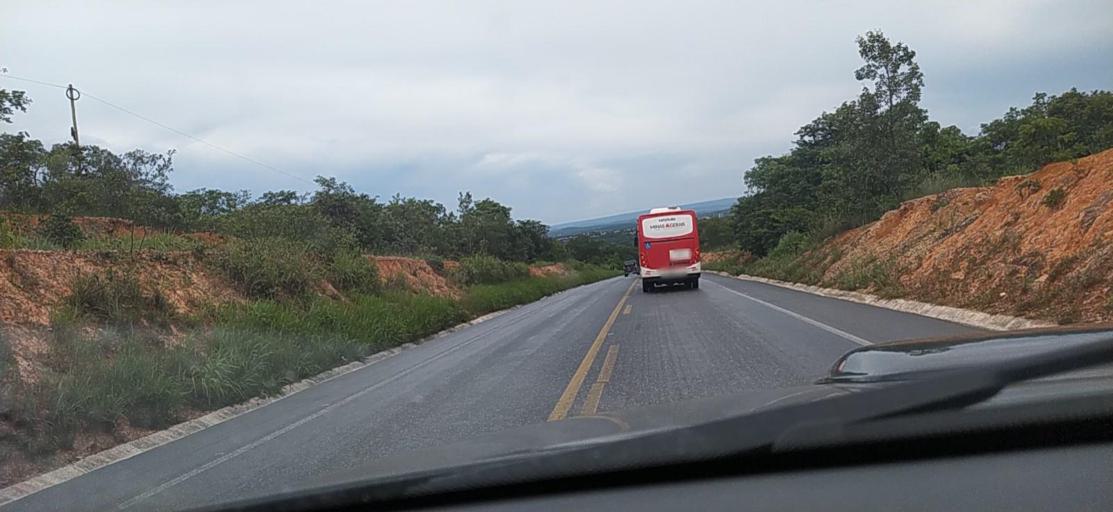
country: BR
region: Minas Gerais
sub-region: Montes Claros
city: Montes Claros
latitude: -16.6622
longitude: -43.7652
